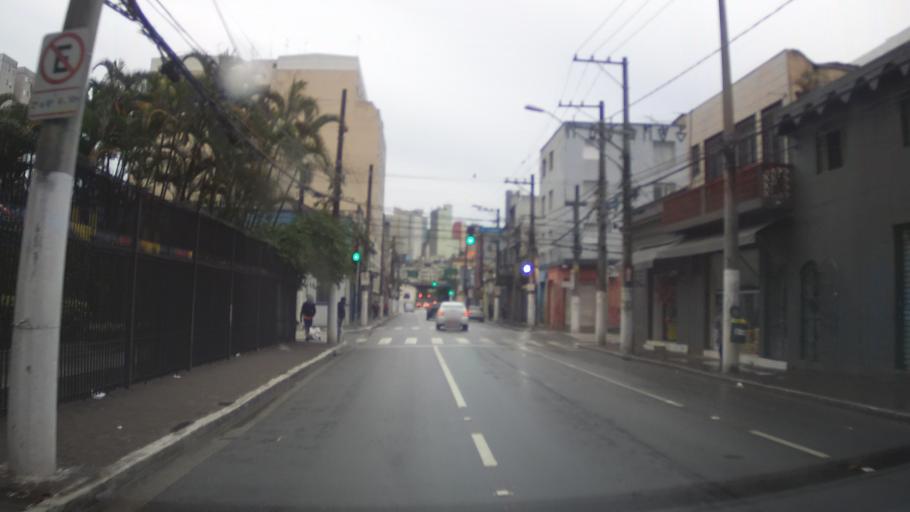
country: BR
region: Sao Paulo
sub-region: Sao Paulo
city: Sao Paulo
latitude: -23.5541
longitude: -46.6220
